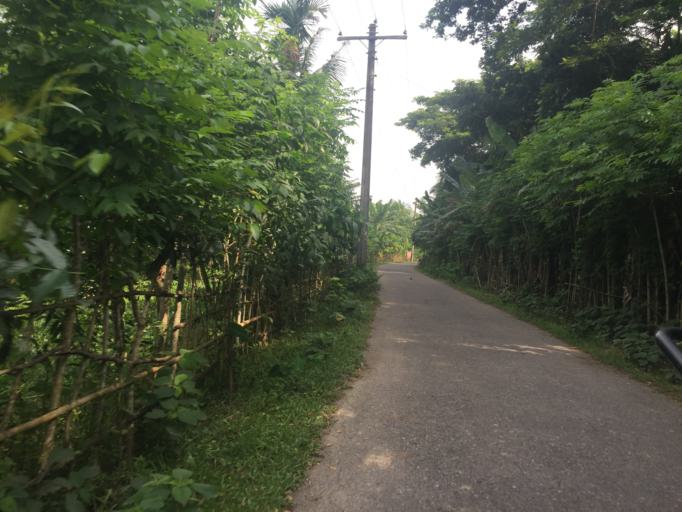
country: BD
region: Barisal
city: Mathba
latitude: 22.2264
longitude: 89.9160
